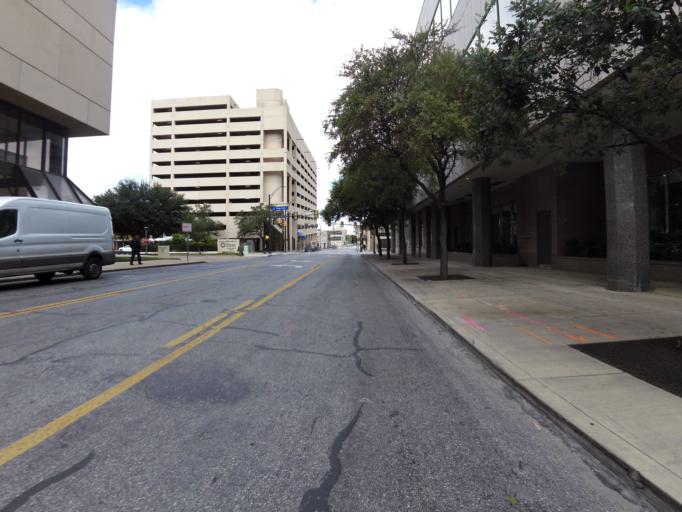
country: US
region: Texas
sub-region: Bexar County
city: San Antonio
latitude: 29.4287
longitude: -98.4933
